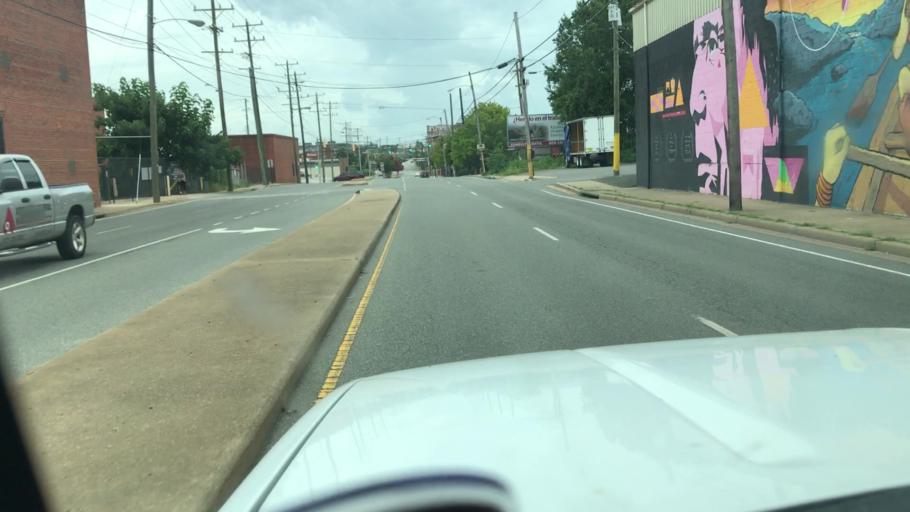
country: US
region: Virginia
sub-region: City of Richmond
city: Richmond
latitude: 37.5666
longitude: -77.4607
